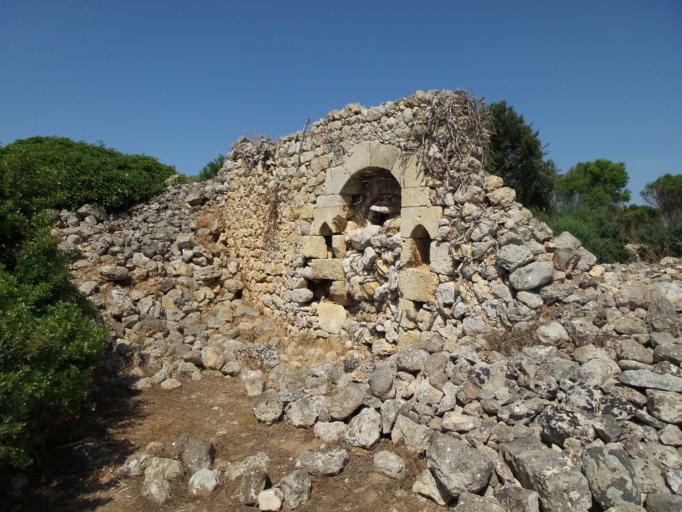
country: ES
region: Balearic Islands
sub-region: Illes Balears
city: Alaior
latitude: 39.9131
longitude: 4.1620
